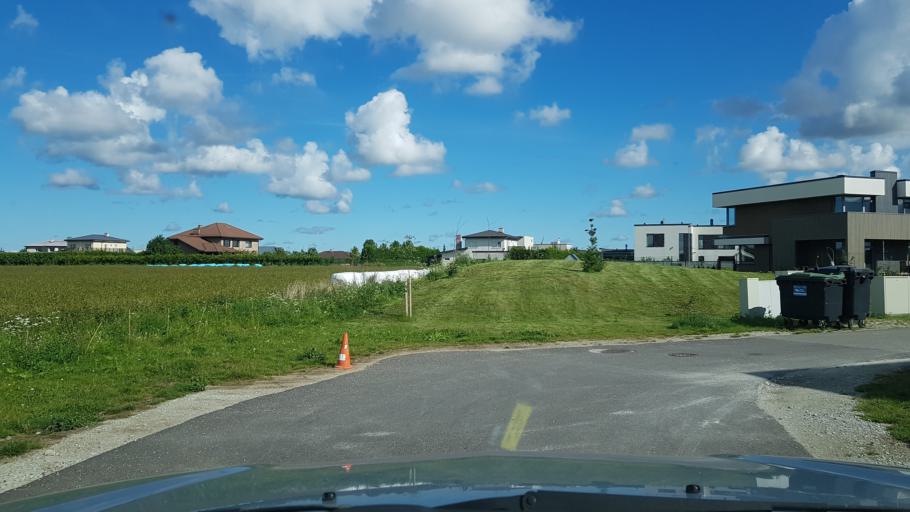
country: EE
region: Harju
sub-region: Tallinna linn
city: Tallinn
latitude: 59.3866
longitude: 24.8029
